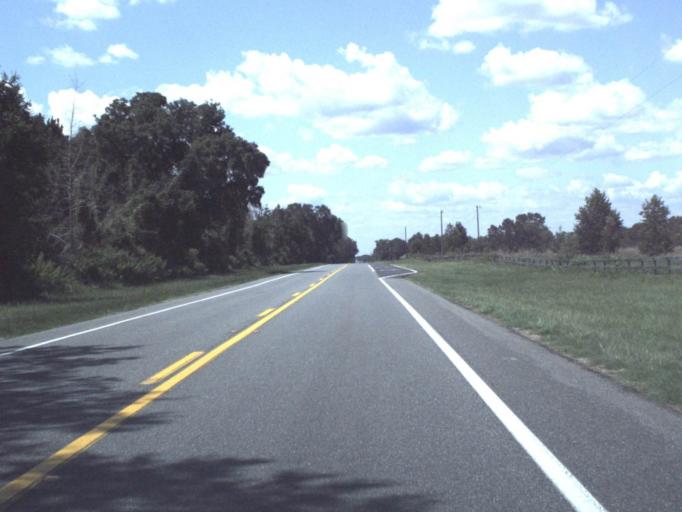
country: US
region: Florida
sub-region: Alachua County
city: High Springs
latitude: 29.9907
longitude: -82.7100
